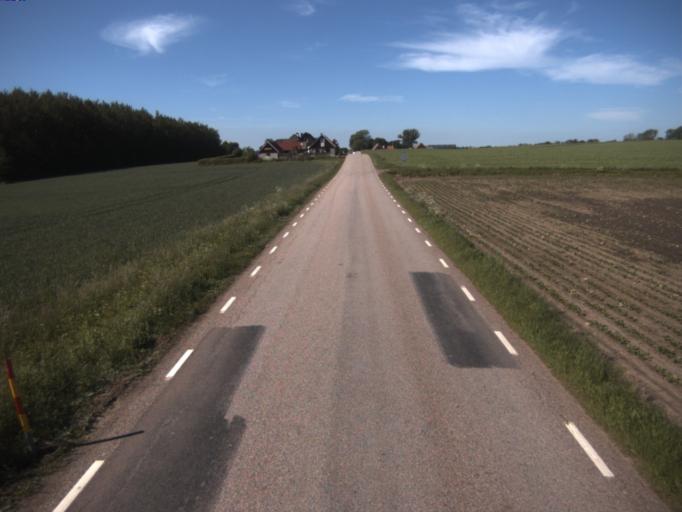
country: SE
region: Skane
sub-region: Helsingborg
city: Gantofta
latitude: 55.9774
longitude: 12.8126
